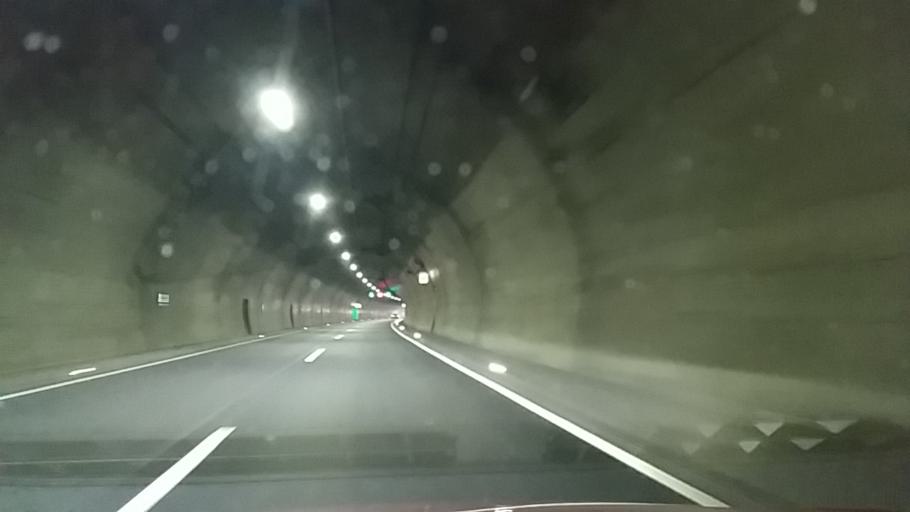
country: DE
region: Thuringia
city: Zella-Mehlis
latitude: 50.6361
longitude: 10.6754
